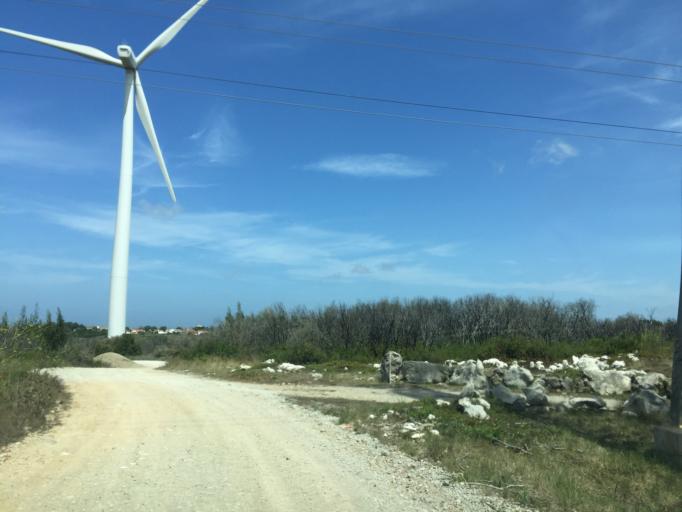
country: PT
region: Leiria
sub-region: Peniche
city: Atouguia da Baleia
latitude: 39.3219
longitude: -9.2608
